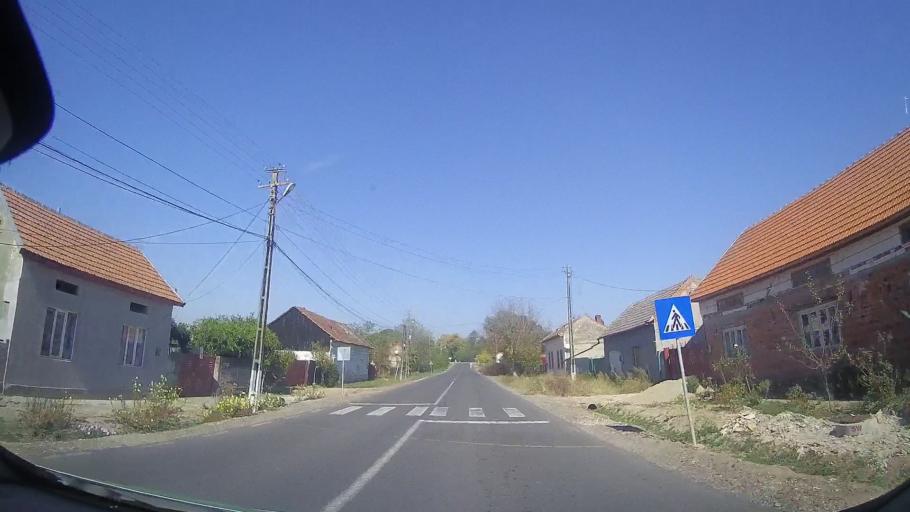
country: RO
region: Timis
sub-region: Comuna Balint
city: Balint
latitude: 45.8100
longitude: 21.8592
